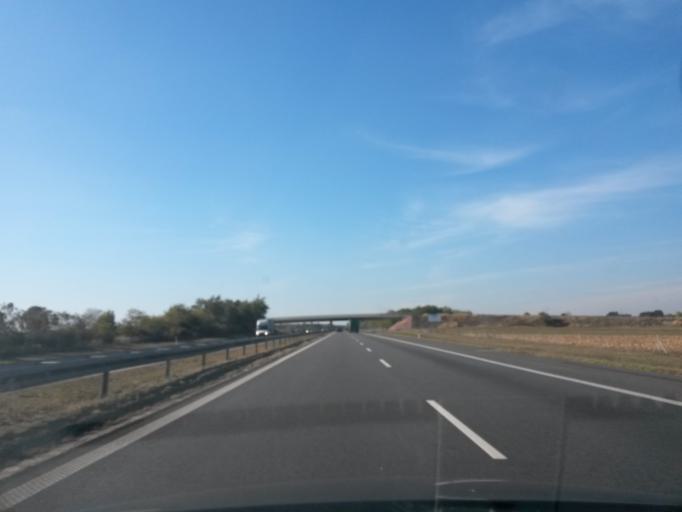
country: PL
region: Opole Voivodeship
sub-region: Powiat opolski
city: Proszkow
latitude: 50.5760
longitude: 17.8465
